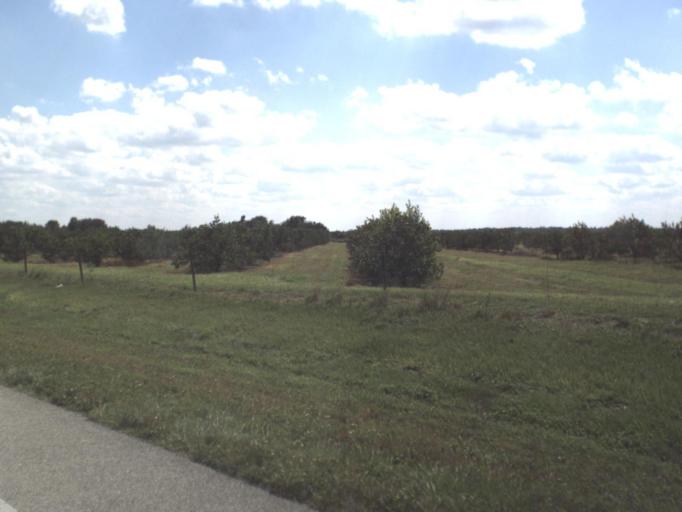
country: US
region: Florida
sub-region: Highlands County
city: Sebring
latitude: 27.4224
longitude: -81.5751
